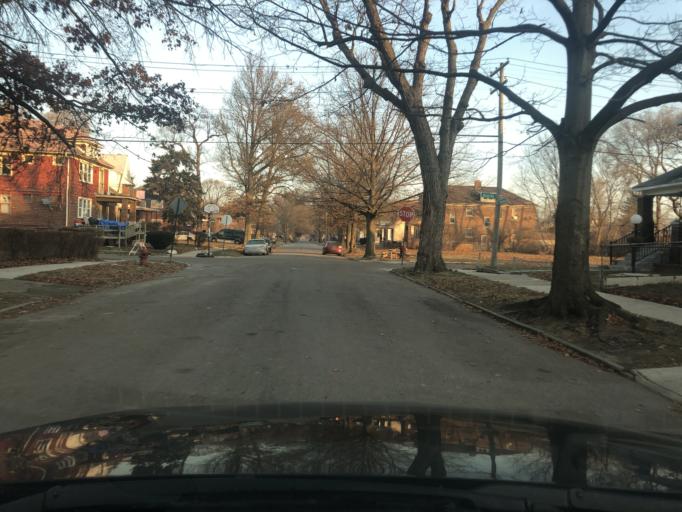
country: US
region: Michigan
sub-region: Wayne County
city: Highland Park
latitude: 42.3986
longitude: -83.1366
